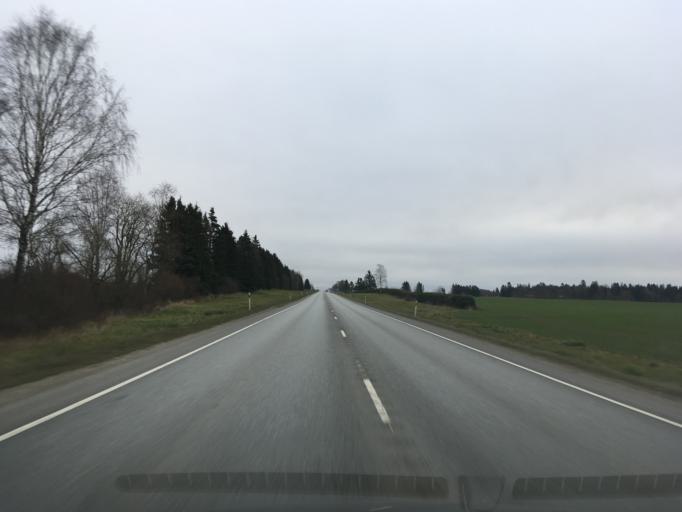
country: EE
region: Laeaene-Virumaa
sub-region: Someru vald
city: Someru
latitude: 59.3653
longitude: 26.4494
